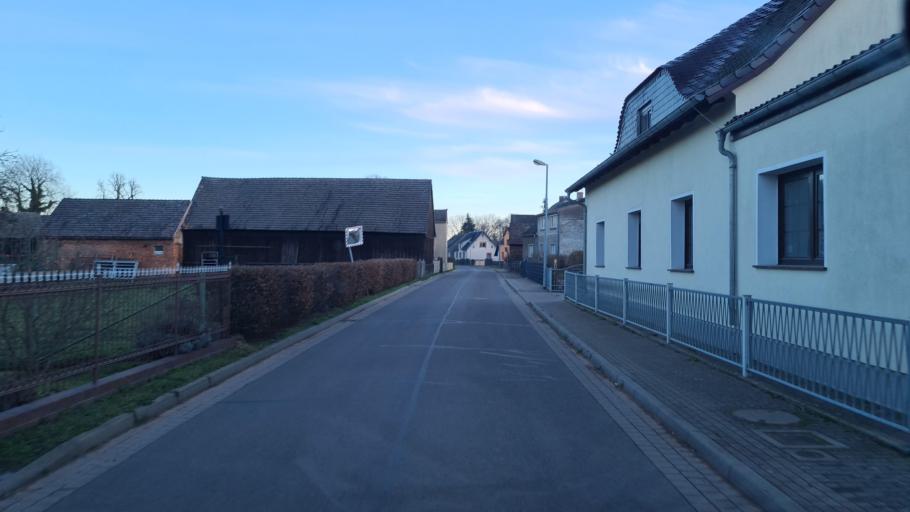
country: DE
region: Brandenburg
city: Burg
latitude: 51.8137
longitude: 14.1328
